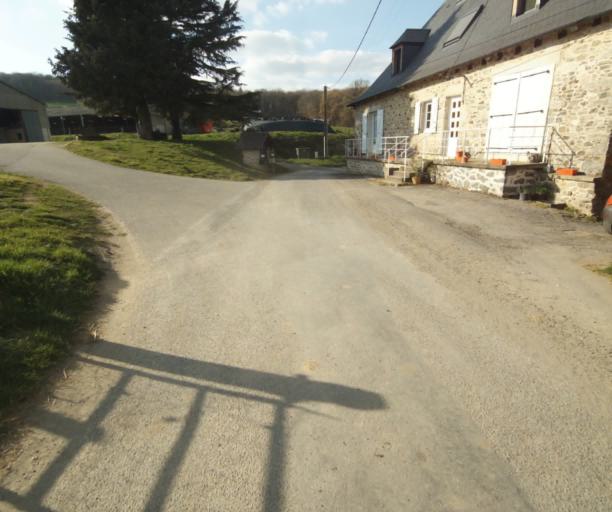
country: FR
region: Limousin
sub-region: Departement de la Correze
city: Saint-Mexant
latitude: 45.3447
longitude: 1.6102
